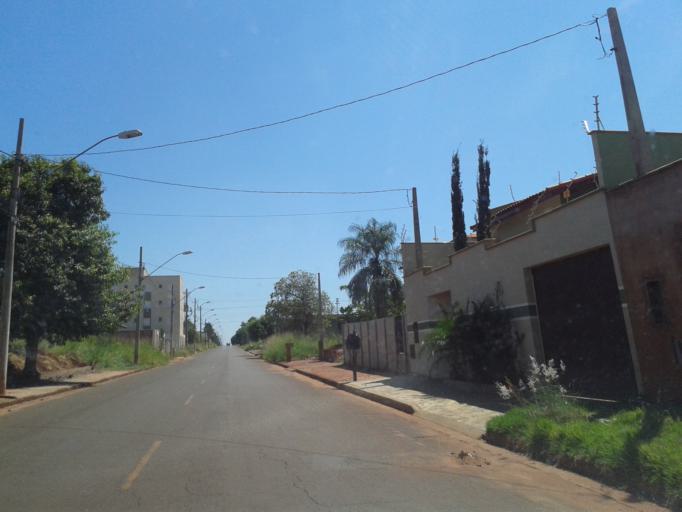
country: BR
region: Minas Gerais
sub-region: Ituiutaba
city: Ituiutaba
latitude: -18.9977
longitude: -49.4551
